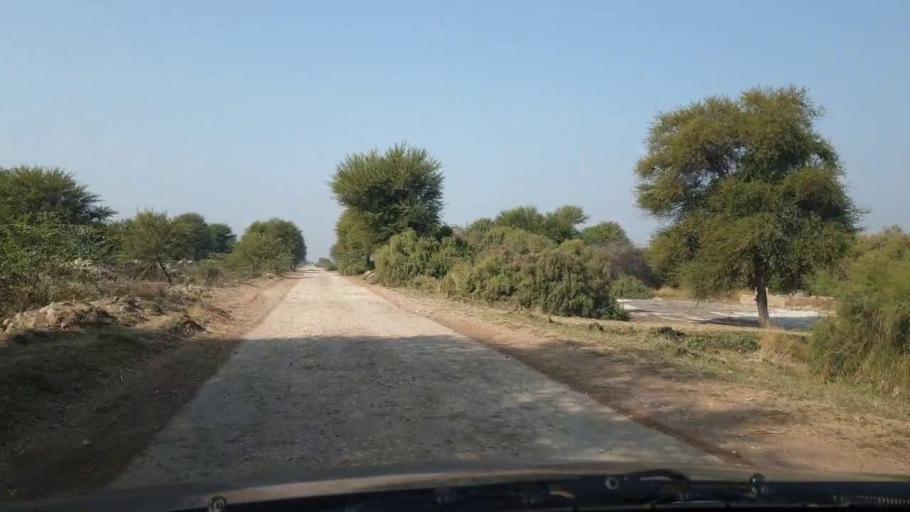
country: PK
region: Sindh
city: Jhol
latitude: 25.9616
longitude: 68.9614
